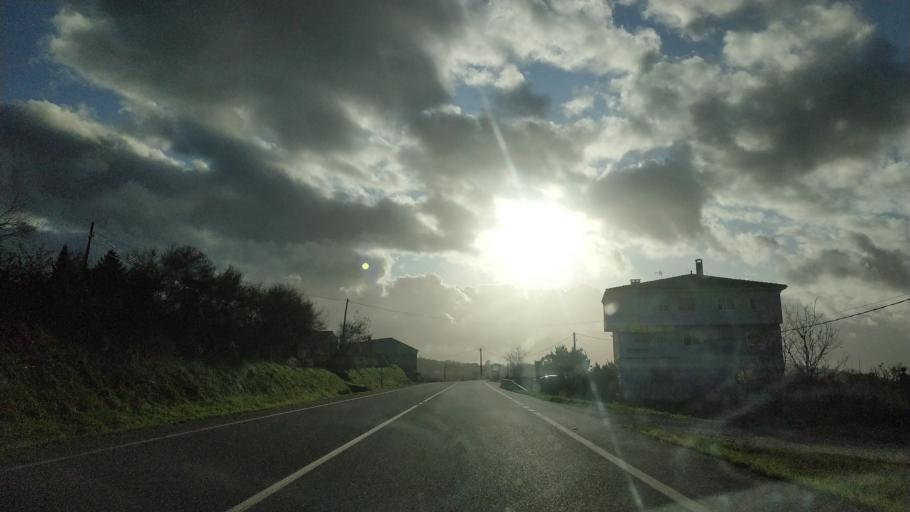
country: ES
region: Galicia
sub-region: Provincia de Pontevedra
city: Silleda
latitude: 42.7851
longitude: -8.1692
